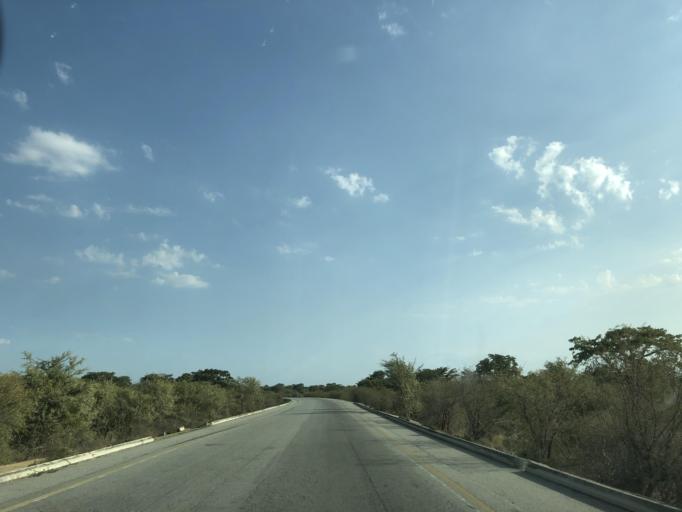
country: AO
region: Benguela
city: Benguela
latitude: -13.2077
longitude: 13.7639
